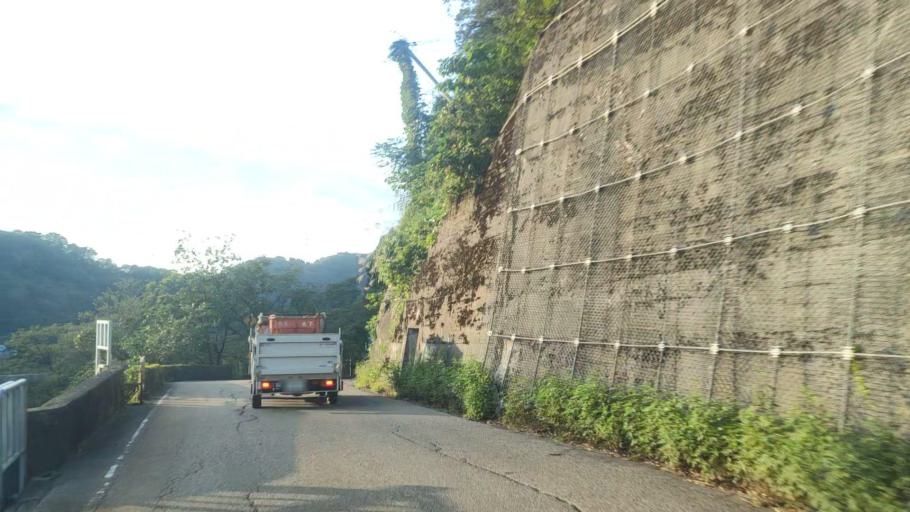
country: JP
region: Toyama
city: Nanto-shi
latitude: 36.5577
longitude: 137.0093
